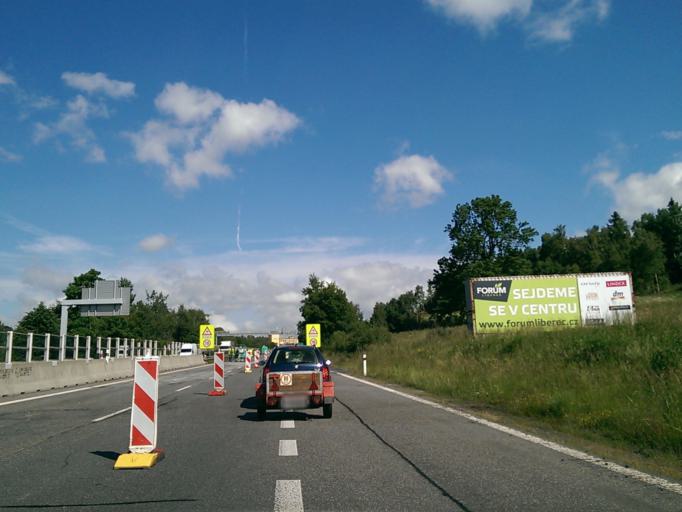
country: CZ
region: Liberecky
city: Hodkovice nad Mohelkou
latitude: 50.7015
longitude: 15.0954
